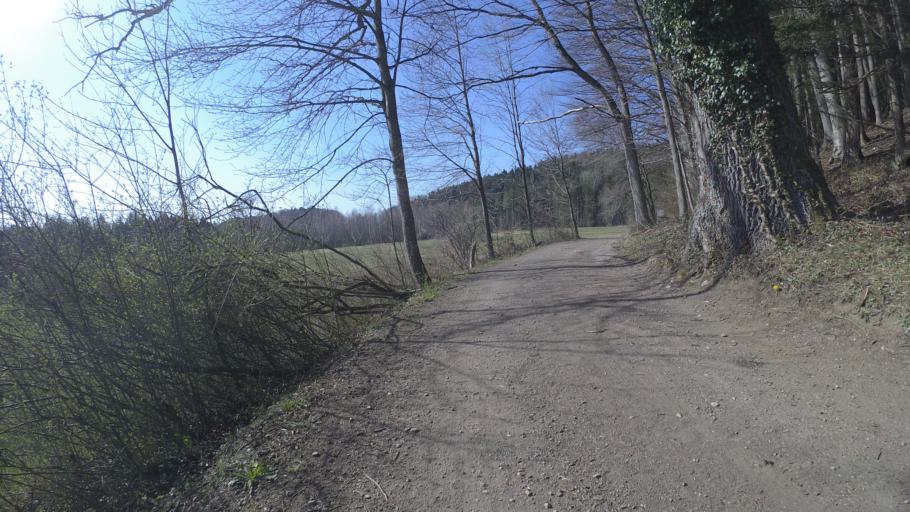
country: DE
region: Bavaria
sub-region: Upper Bavaria
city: Nussdorf
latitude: 47.9043
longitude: 12.5818
